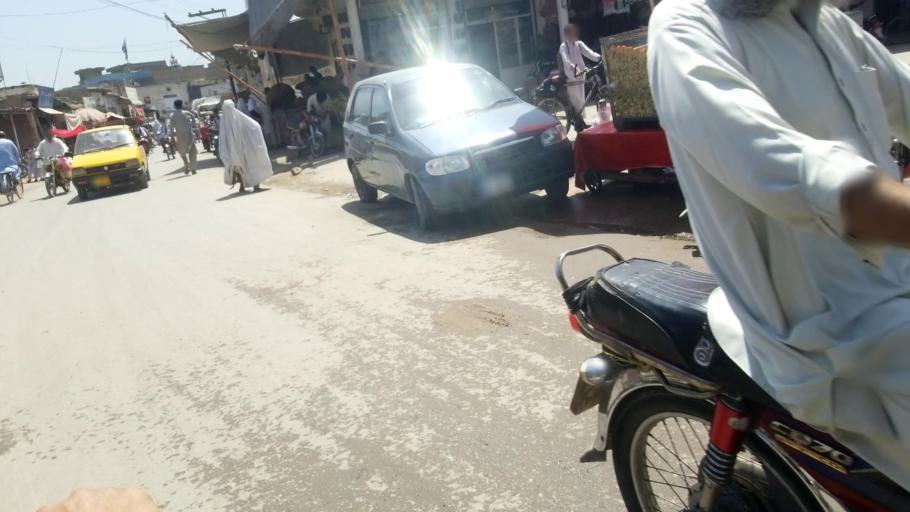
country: PK
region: Khyber Pakhtunkhwa
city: Peshawar
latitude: 34.0291
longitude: 71.4881
